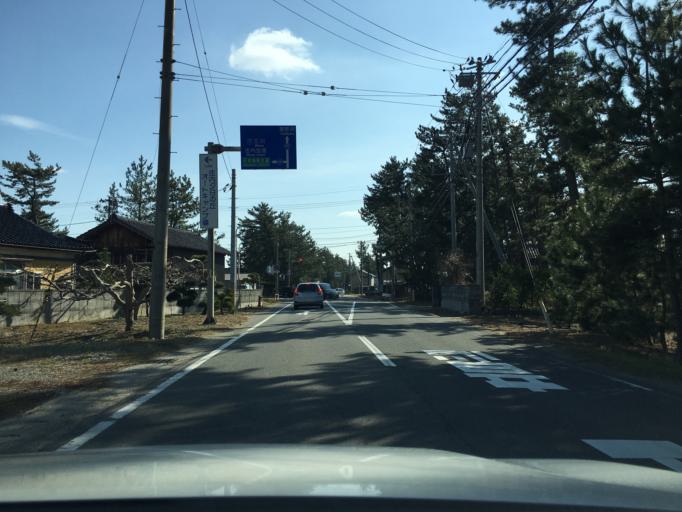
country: JP
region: Yamagata
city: Tsuruoka
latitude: 38.8205
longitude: 139.7787
